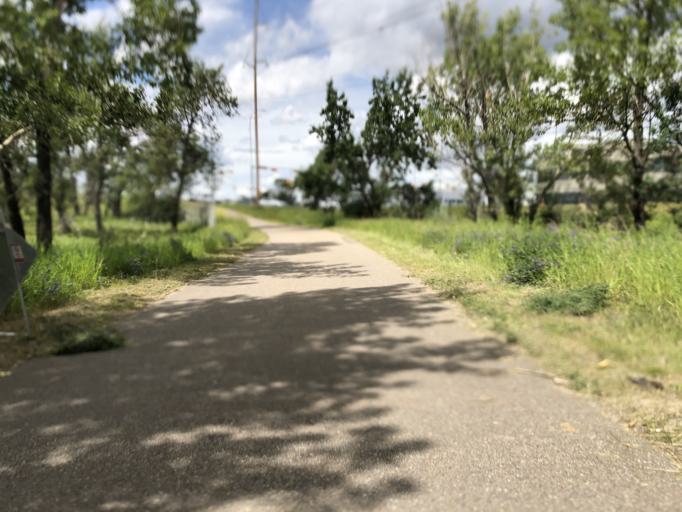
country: CA
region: Alberta
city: Calgary
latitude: 50.9866
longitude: -114.0276
